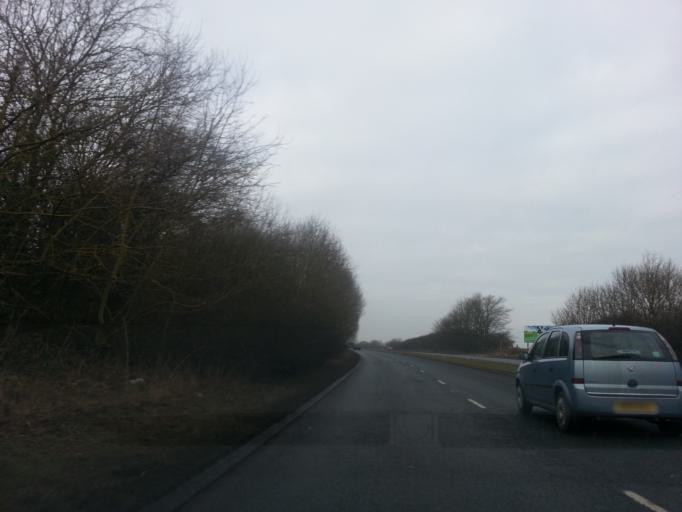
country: GB
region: England
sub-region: Darlington
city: Heighington
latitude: 54.5660
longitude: -1.6014
